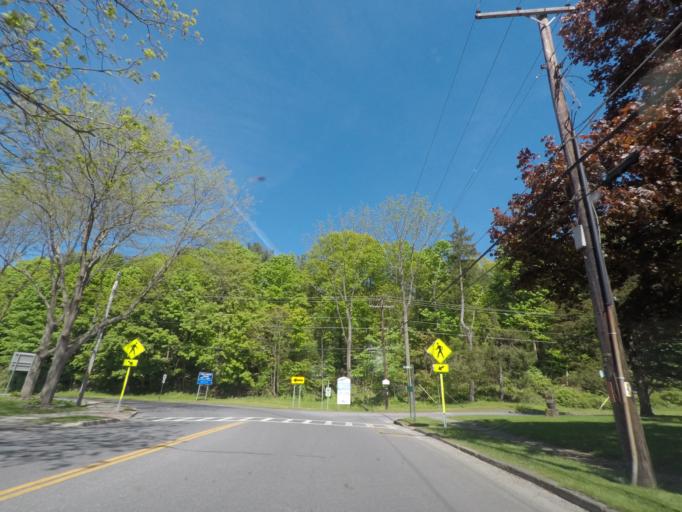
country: US
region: New York
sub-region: Ulster County
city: Saugerties
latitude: 42.0802
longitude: -73.9444
